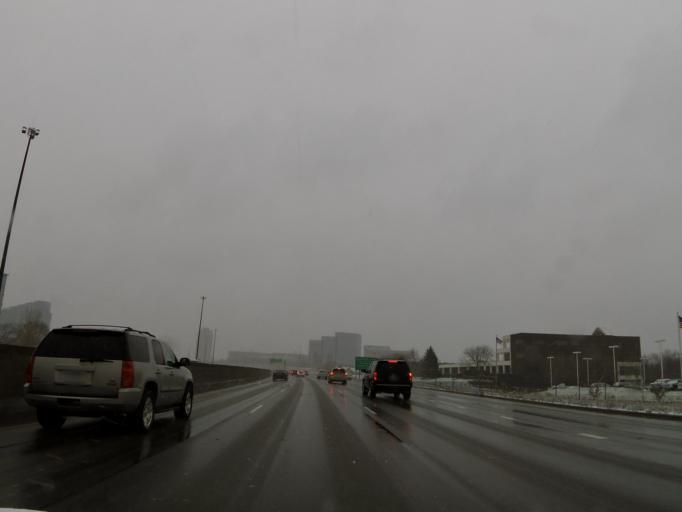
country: US
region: Minnesota
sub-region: Hennepin County
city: Edina
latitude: 44.8579
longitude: -93.3390
